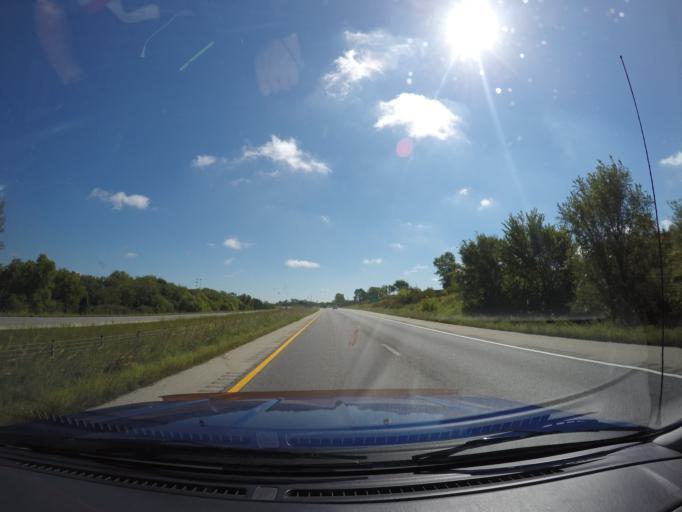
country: US
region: Kansas
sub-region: Johnson County
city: Olathe
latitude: 38.9428
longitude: -94.8704
